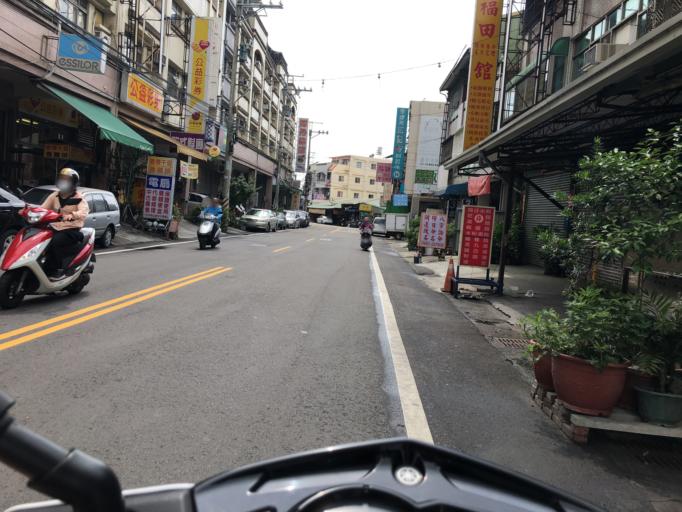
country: TW
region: Taiwan
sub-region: Taichung City
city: Taichung
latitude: 24.0861
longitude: 120.7111
